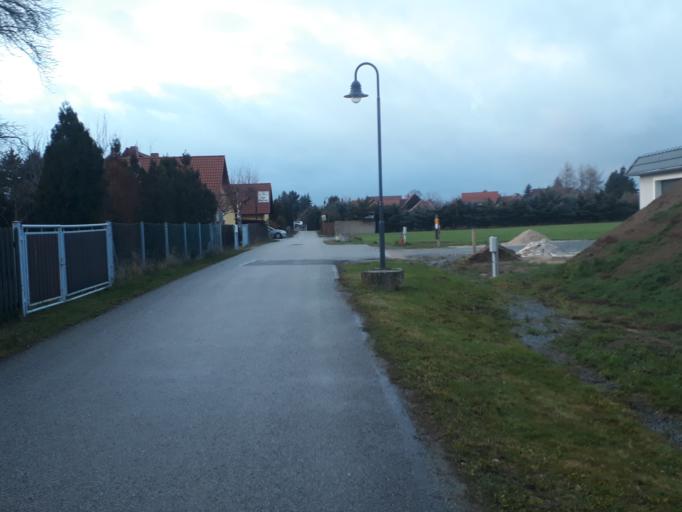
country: DE
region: Saxony
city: Guttau
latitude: 51.2591
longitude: 14.5550
